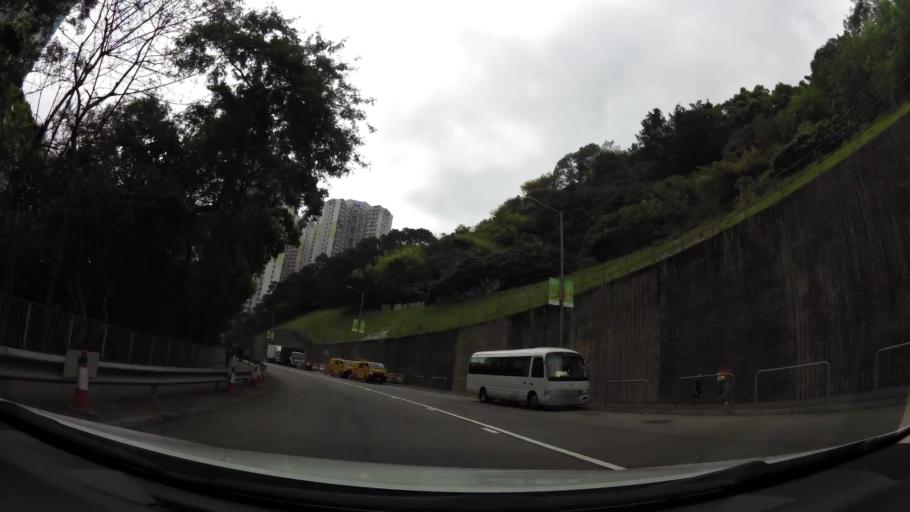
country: HK
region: Wanchai
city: Wan Chai
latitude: 22.2790
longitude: 114.2189
